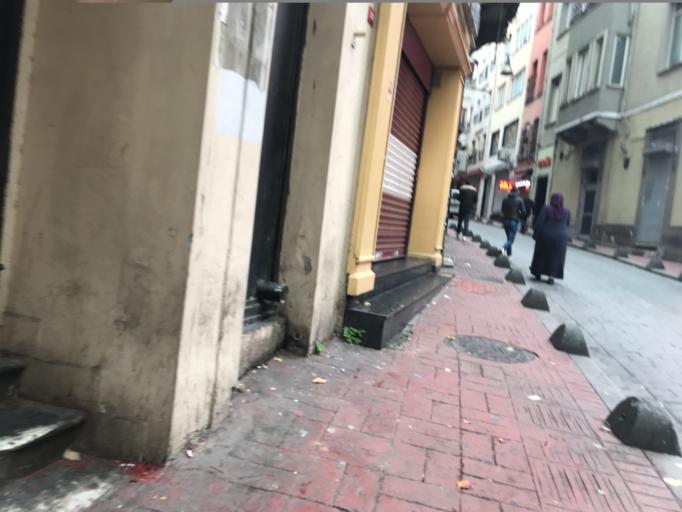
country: TR
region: Istanbul
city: Eminoenue
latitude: 41.0350
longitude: 28.9785
